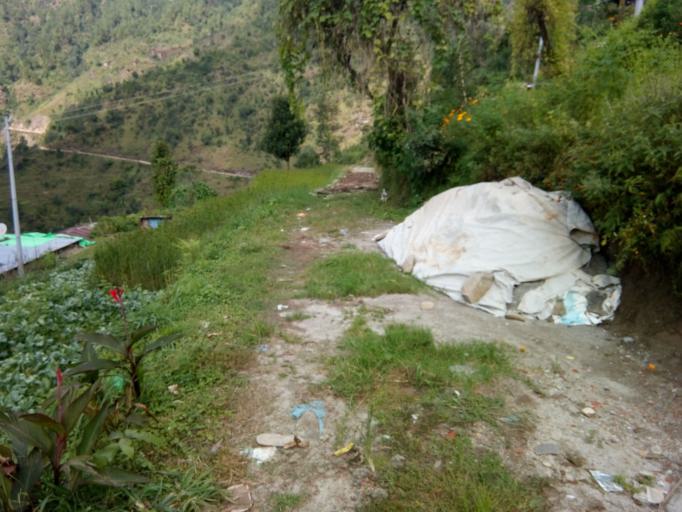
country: NP
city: Kodari
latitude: 27.7035
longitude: 85.9214
